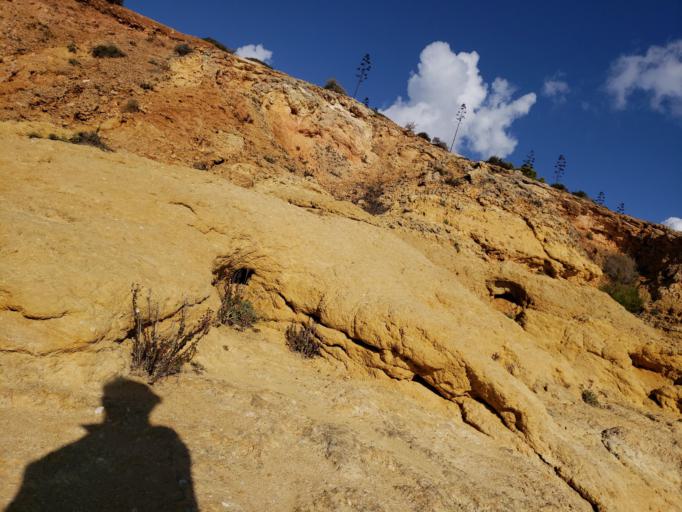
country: PT
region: Faro
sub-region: Lagoa
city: Carvoeiro
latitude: 37.0927
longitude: -8.4646
